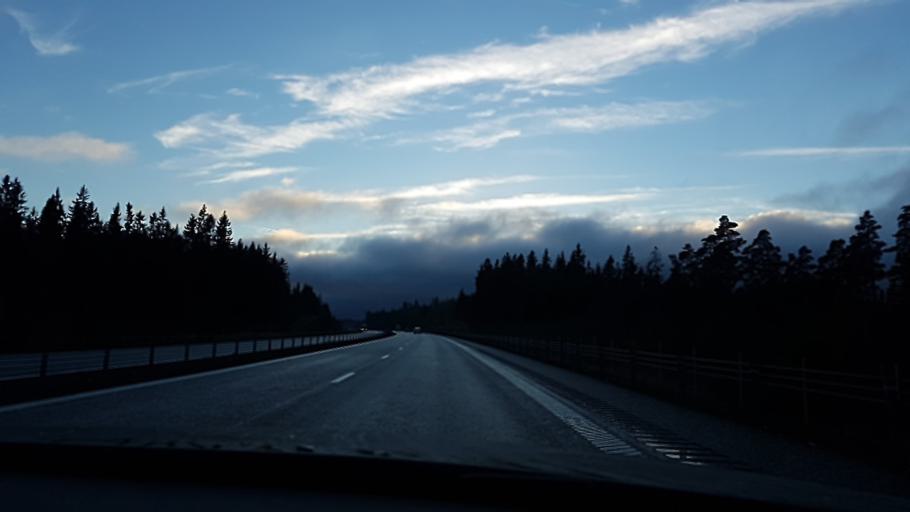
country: SE
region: Kronoberg
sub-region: Markaryds Kommun
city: Markaryd
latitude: 56.4220
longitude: 13.5531
